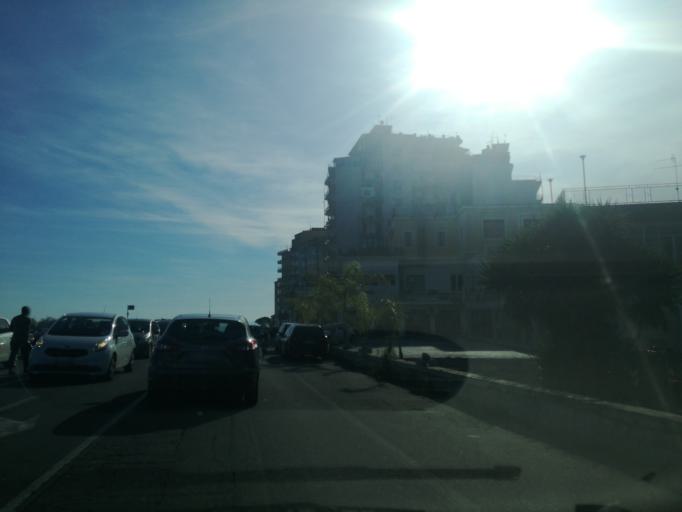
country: IT
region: Sicily
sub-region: Catania
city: Acireale
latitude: 37.6190
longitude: 15.1696
